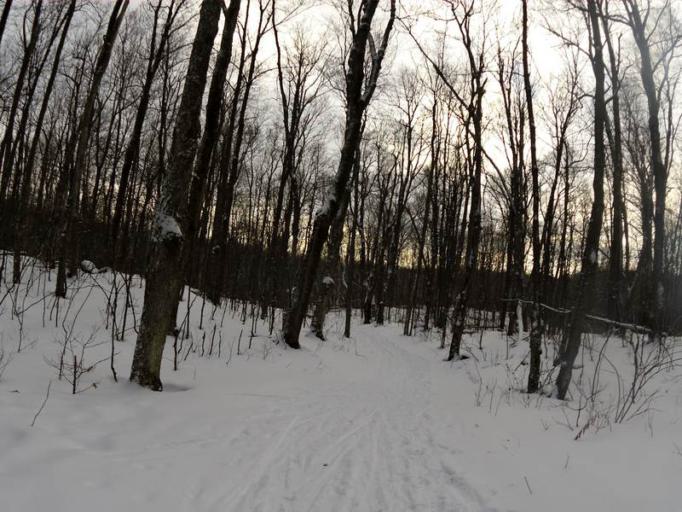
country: CA
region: Quebec
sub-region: Outaouais
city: Wakefield
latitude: 45.5223
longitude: -75.9133
